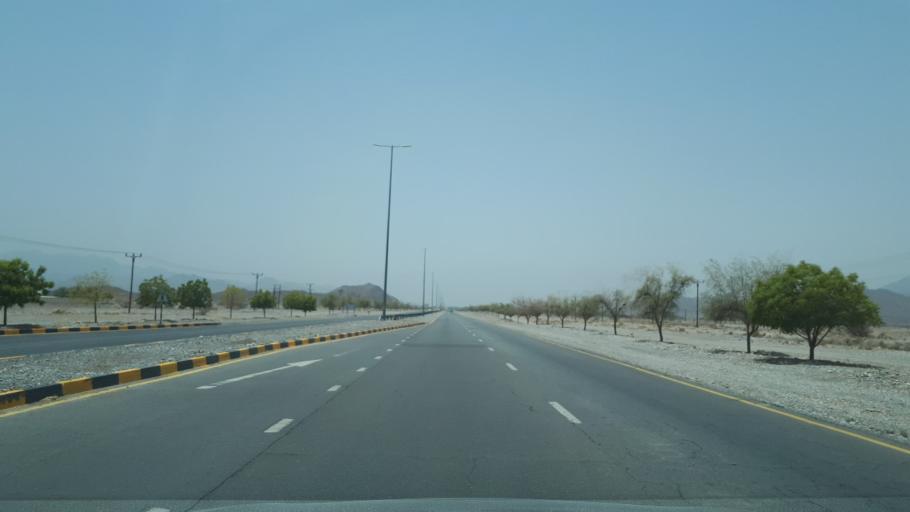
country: OM
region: Al Batinah
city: Rustaq
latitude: 23.5165
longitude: 57.4621
